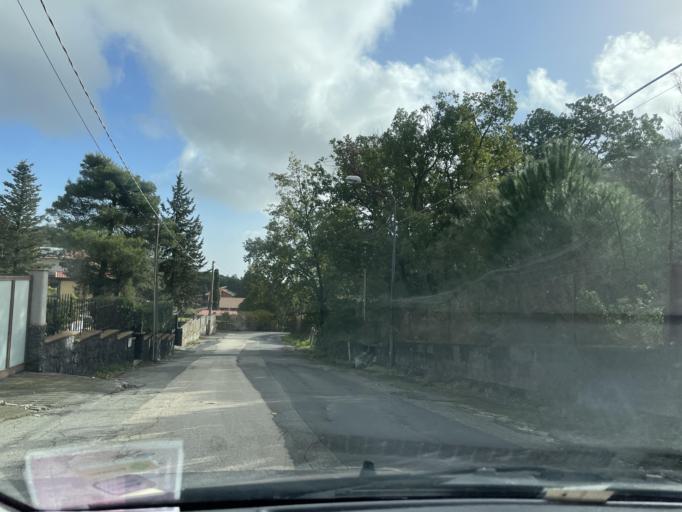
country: IT
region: Sicily
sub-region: Catania
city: Nicolosi
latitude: 37.6286
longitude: 15.0211
